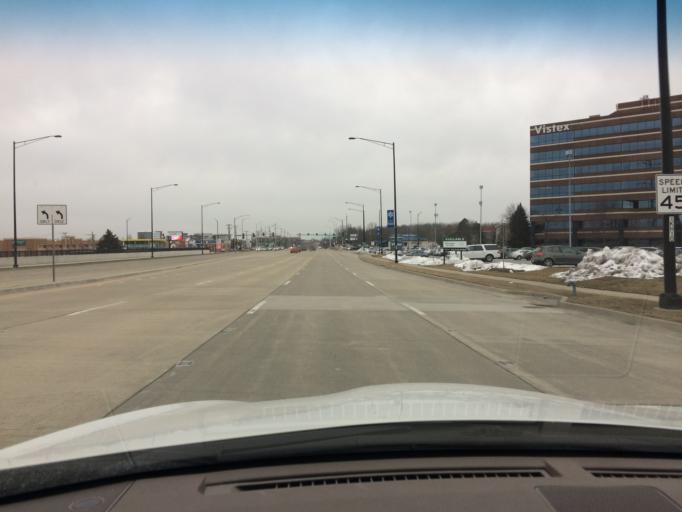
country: US
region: Illinois
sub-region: Cook County
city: South Barrington
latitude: 42.0651
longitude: -88.1447
